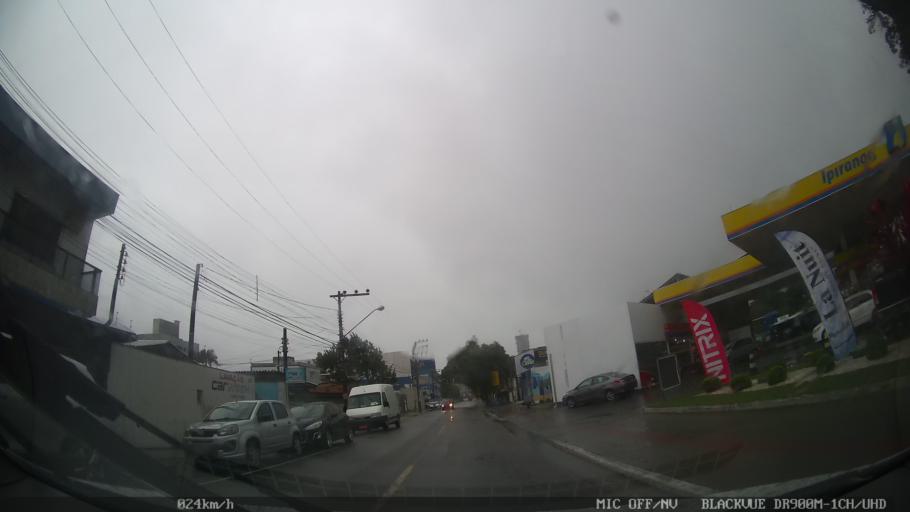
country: BR
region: Santa Catarina
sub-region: Balneario Camboriu
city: Balneario Camboriu
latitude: -27.0113
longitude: -48.6263
